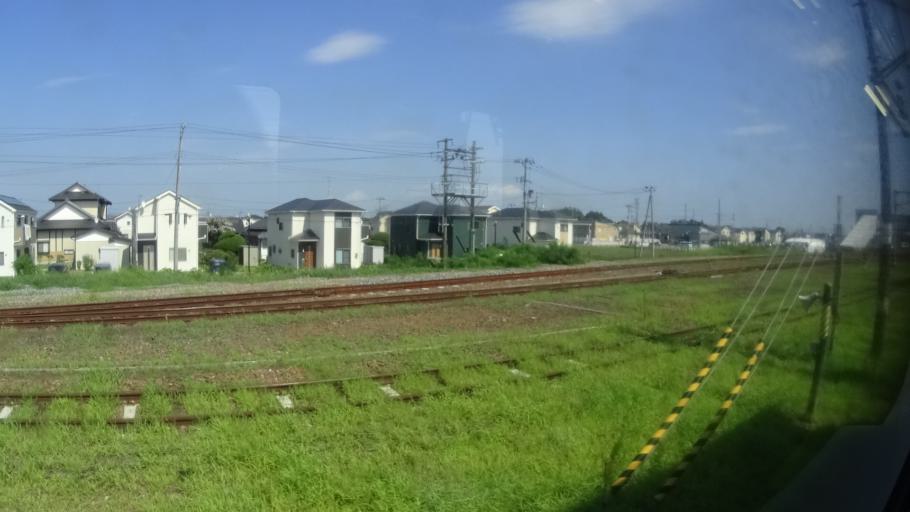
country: JP
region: Miyagi
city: Kogota
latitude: 38.5427
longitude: 141.0644
